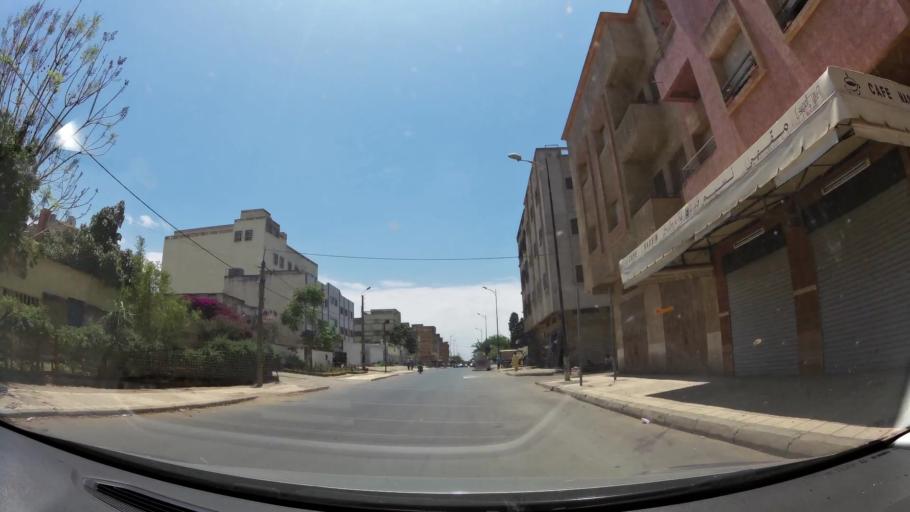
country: MA
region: Gharb-Chrarda-Beni Hssen
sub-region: Kenitra Province
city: Kenitra
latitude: 34.2371
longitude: -6.6179
